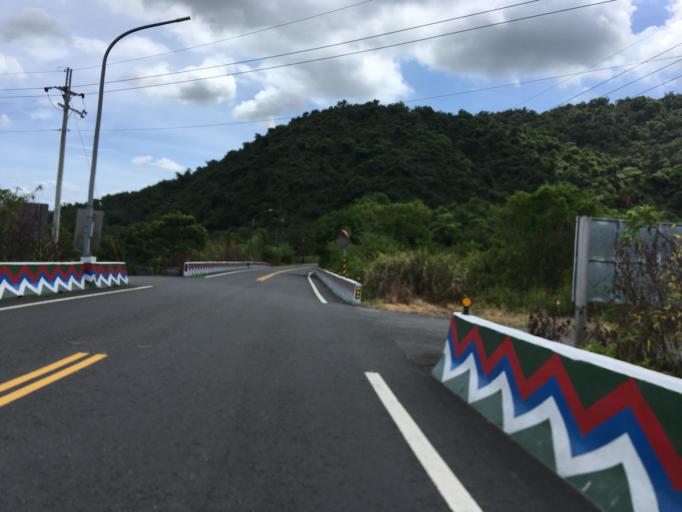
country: TW
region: Taiwan
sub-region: Yilan
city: Yilan
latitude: 24.6238
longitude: 121.7070
